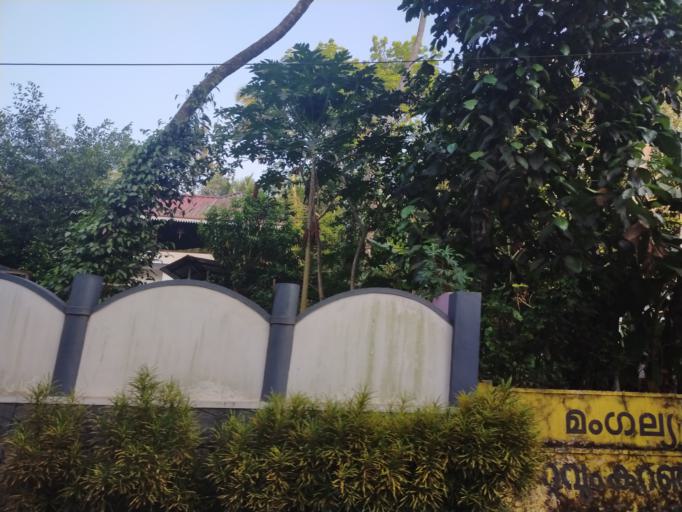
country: IN
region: Kerala
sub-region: Kottayam
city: Palackattumala
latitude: 9.7451
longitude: 76.5135
